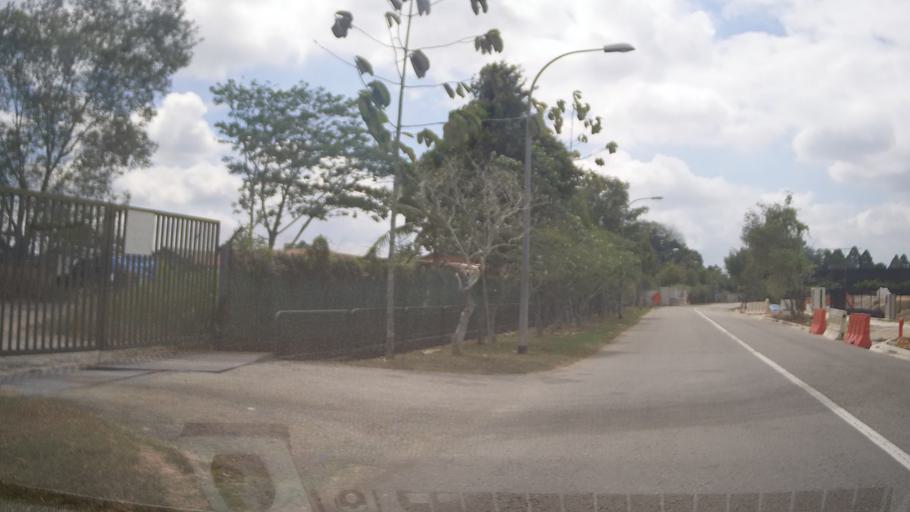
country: MY
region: Johor
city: Johor Bahru
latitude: 1.4421
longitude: 103.7320
